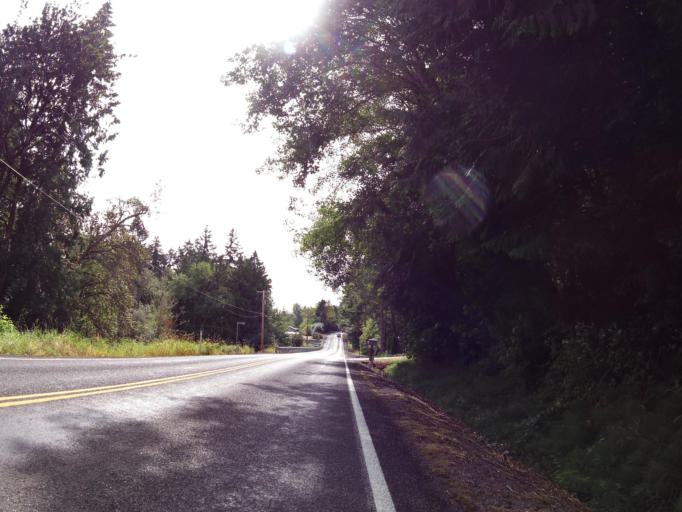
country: US
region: Washington
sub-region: Lewis County
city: Chehalis
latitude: 46.6317
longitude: -122.9694
